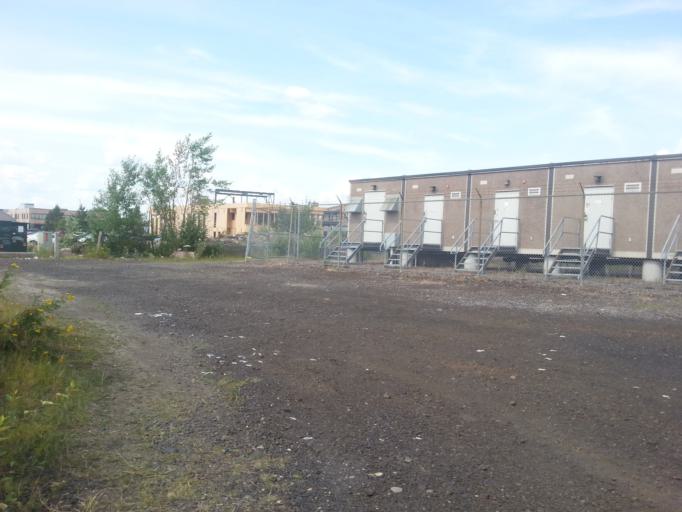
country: CA
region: Ontario
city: Greater Sudbury
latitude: 46.4913
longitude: -80.9976
